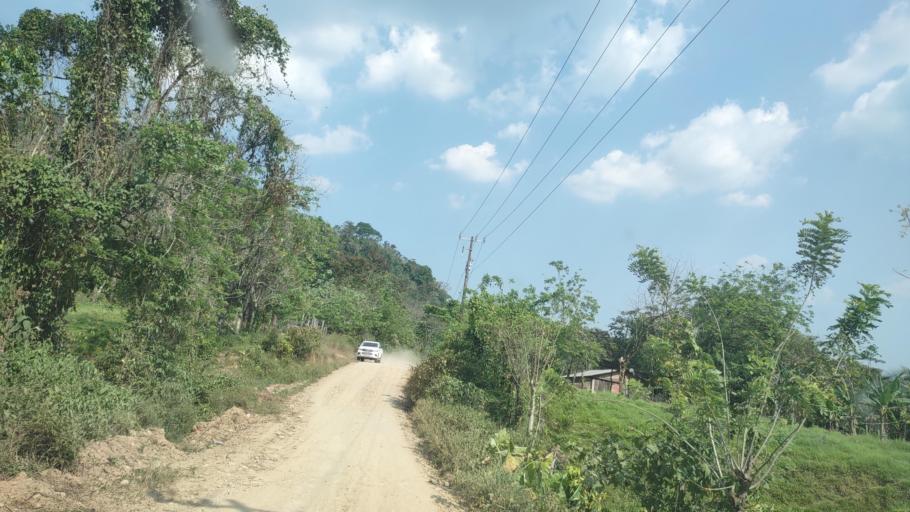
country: MX
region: Chiapas
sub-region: Tecpatan
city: Raudales Malpaso
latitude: 17.3316
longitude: -93.7492
